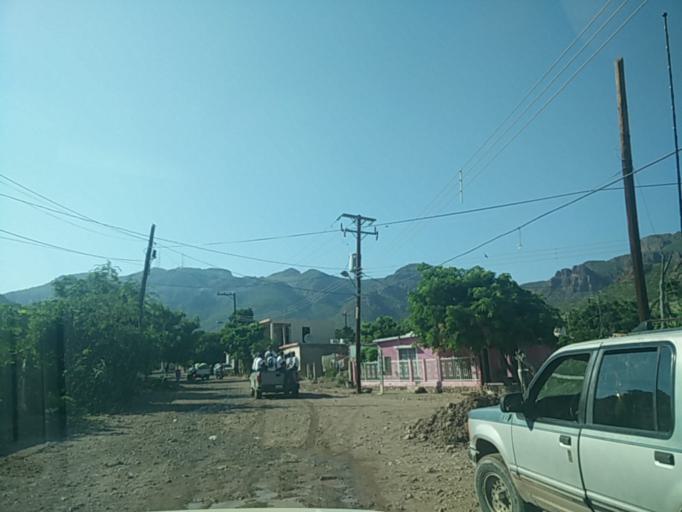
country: MX
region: Sonora
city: Heroica Guaymas
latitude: 27.9369
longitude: -110.8808
